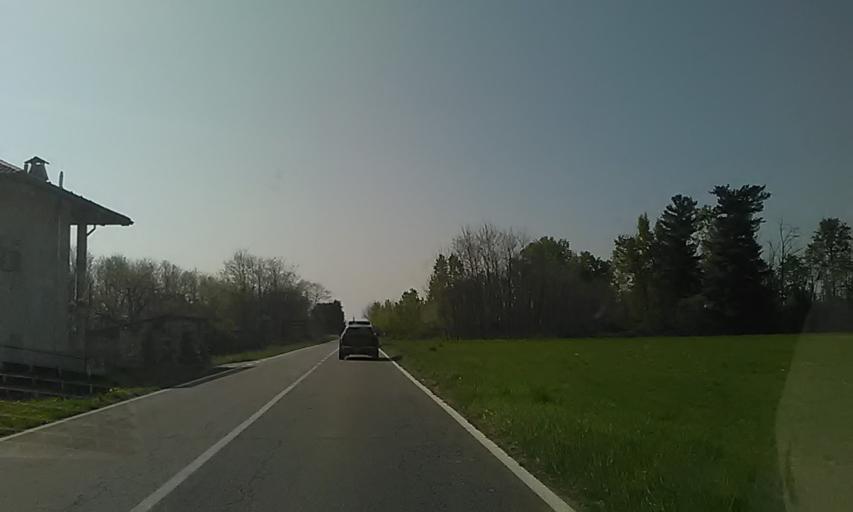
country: IT
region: Piedmont
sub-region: Provincia di Vercelli
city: Ghislarengo
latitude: 45.5140
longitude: 8.3875
